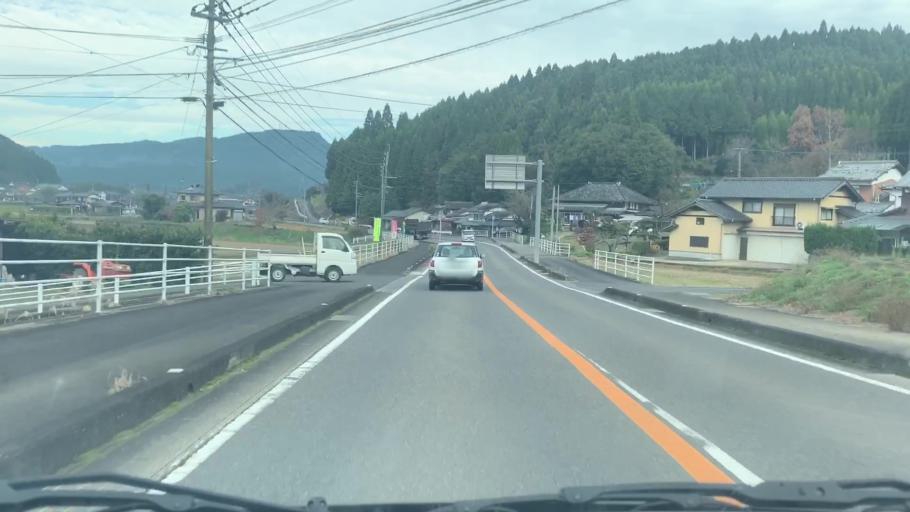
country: JP
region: Saga Prefecture
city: Imaricho-ko
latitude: 33.2646
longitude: 129.9657
